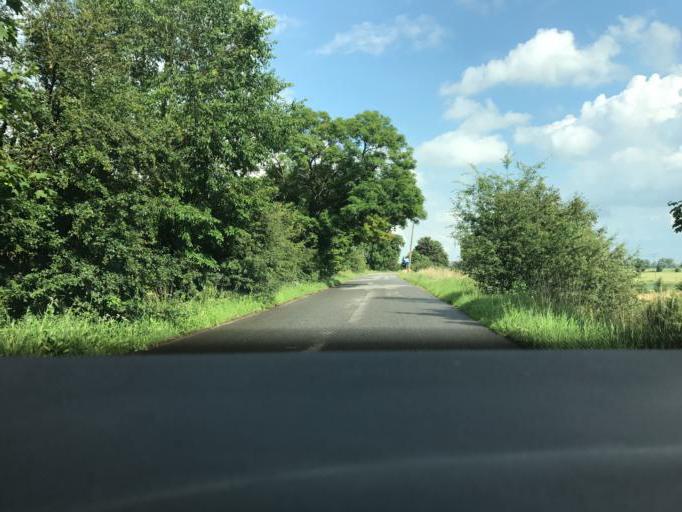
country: PL
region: Pomeranian Voivodeship
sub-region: Powiat gdanski
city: Cedry Wielkie
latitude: 54.3366
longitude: 18.8074
